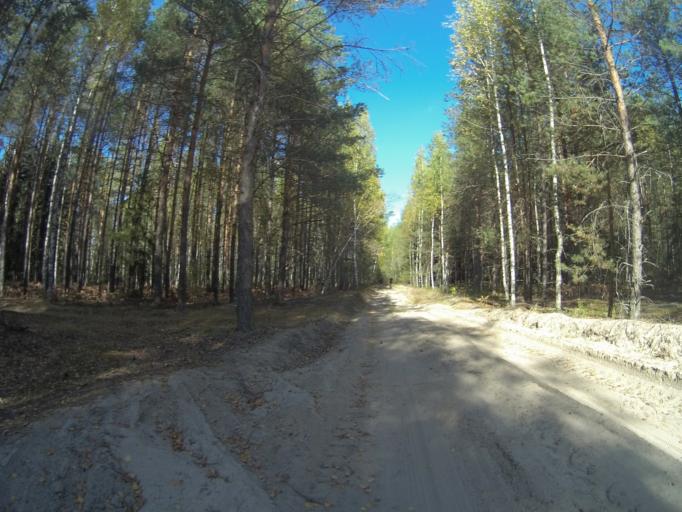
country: RU
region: Vladimir
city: Vorsha
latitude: 55.8955
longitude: 40.1741
